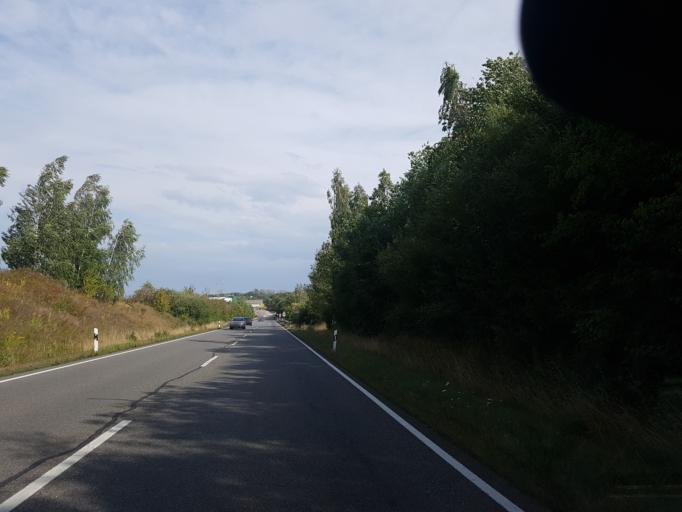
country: DE
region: Saxony
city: Grossweitzschen
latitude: 51.1286
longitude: 13.0444
